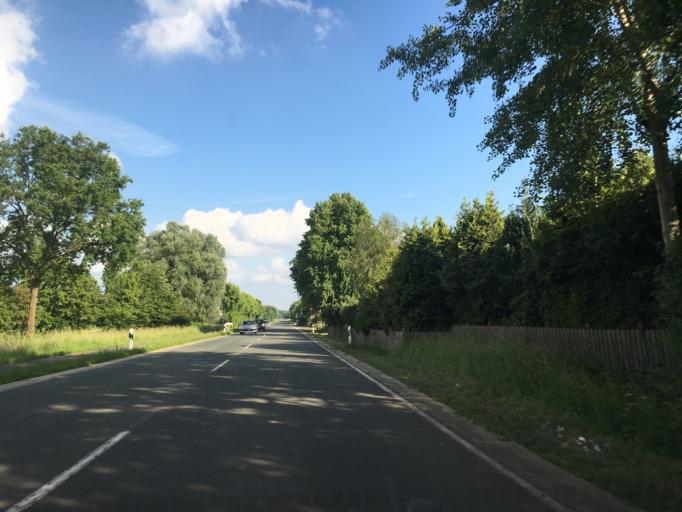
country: DE
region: North Rhine-Westphalia
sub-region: Regierungsbezirk Munster
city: Altenberge
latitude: 52.0679
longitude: 7.4432
